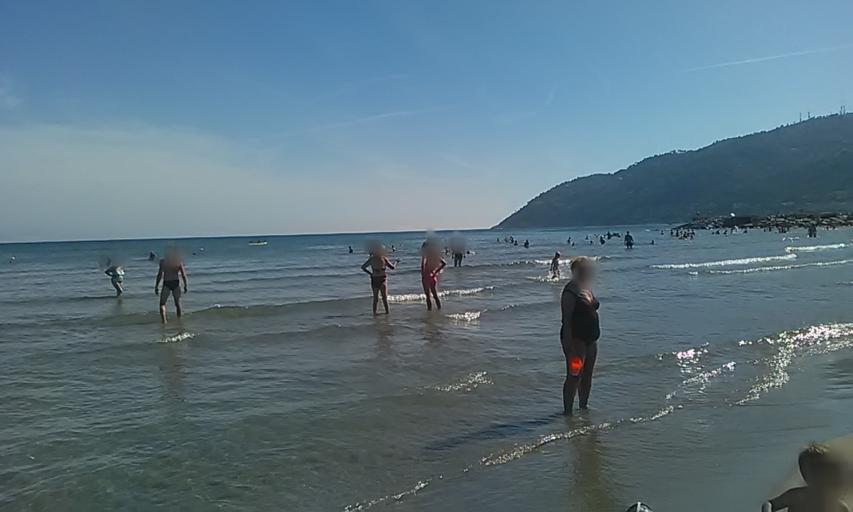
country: IT
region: Liguria
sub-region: Provincia di Savona
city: Marina di Andora
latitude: 43.9512
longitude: 8.1540
